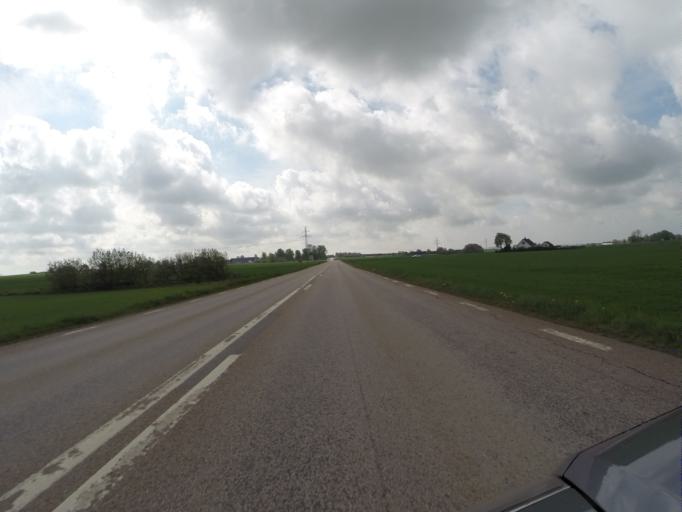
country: SE
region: Skane
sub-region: Landskrona
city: Asmundtorp
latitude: 55.9740
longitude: 12.9388
